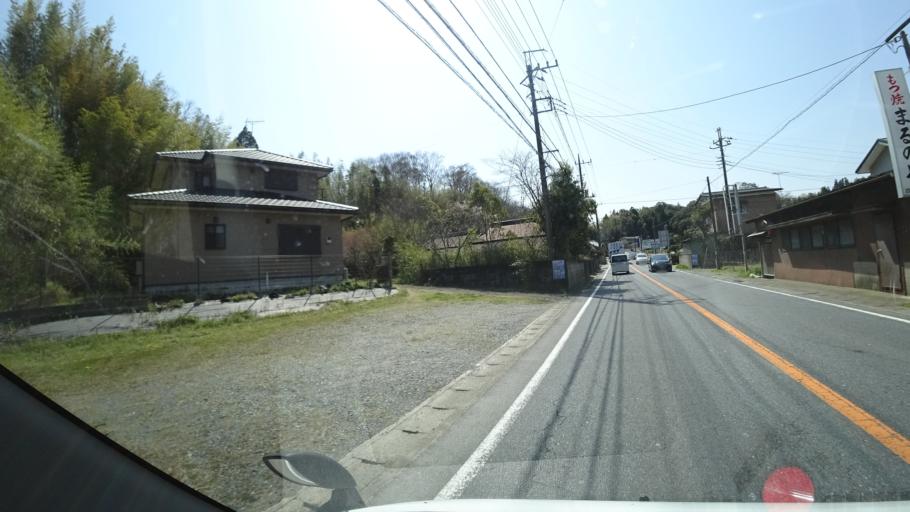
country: JP
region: Chiba
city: Narita
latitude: 35.8059
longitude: 140.3118
